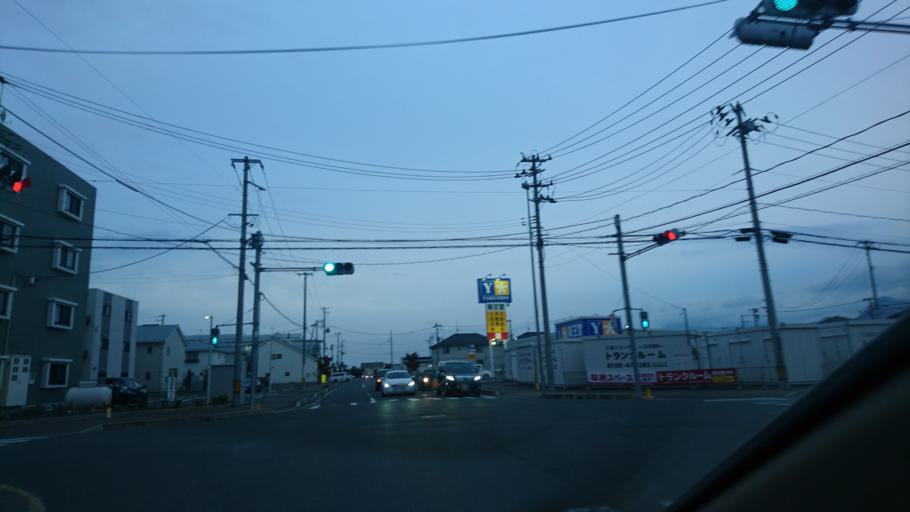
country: JP
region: Iwate
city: Morioka-shi
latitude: 39.6727
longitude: 141.1321
